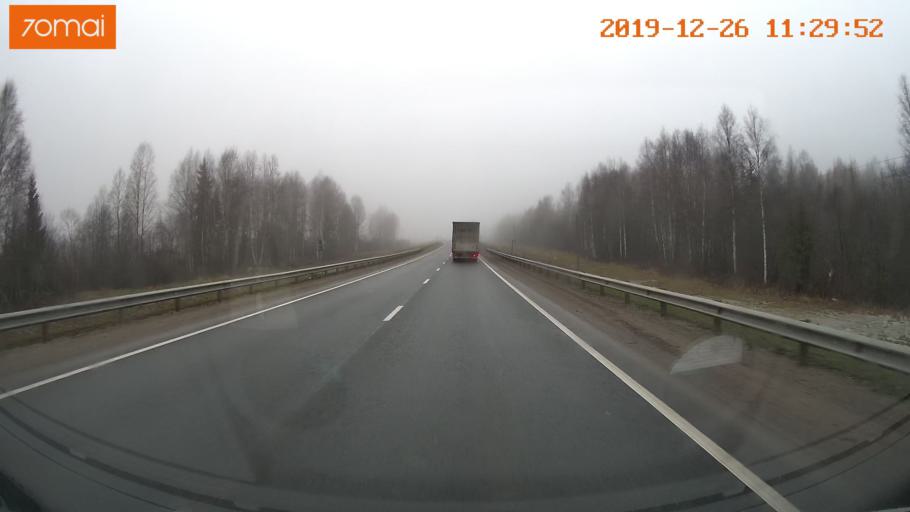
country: RU
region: Vologda
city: Chebsara
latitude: 59.1624
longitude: 38.7853
